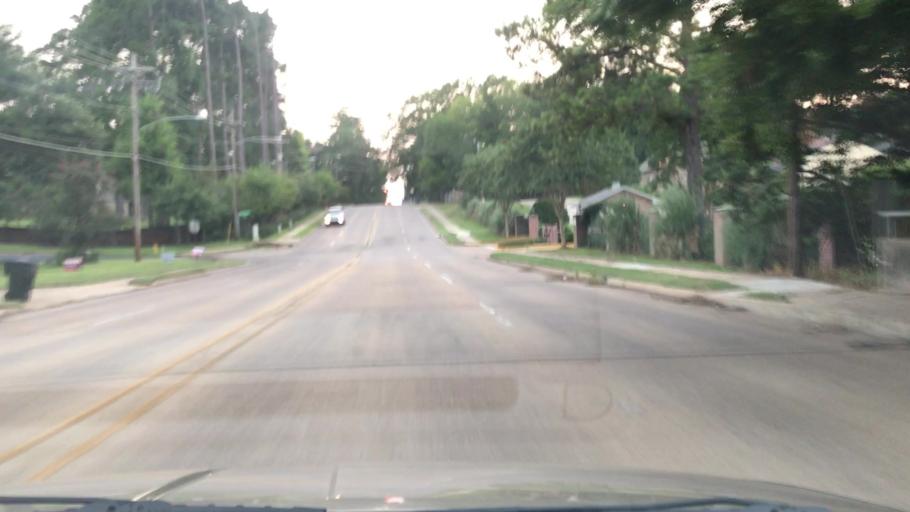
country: US
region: Louisiana
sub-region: Bossier Parish
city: Bossier City
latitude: 32.4547
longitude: -93.7348
